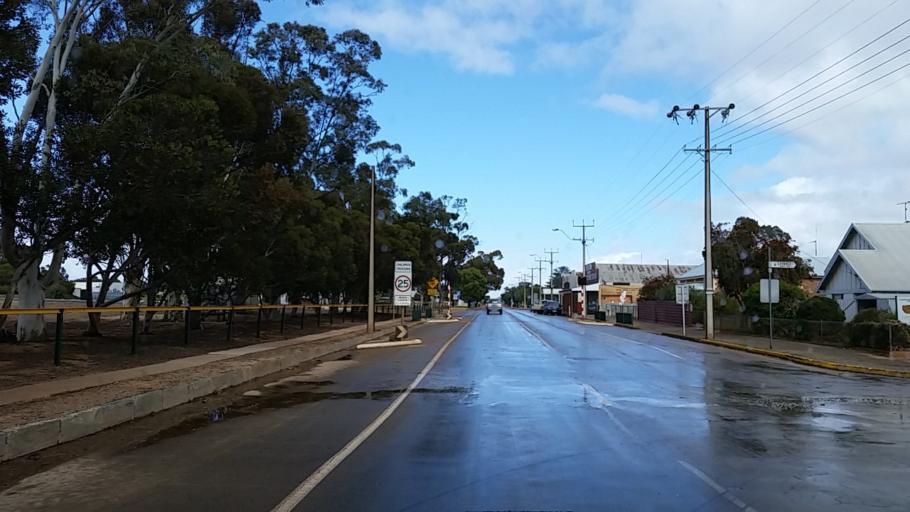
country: AU
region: South Australia
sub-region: Peterborough
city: Peterborough
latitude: -32.9737
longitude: 138.8336
